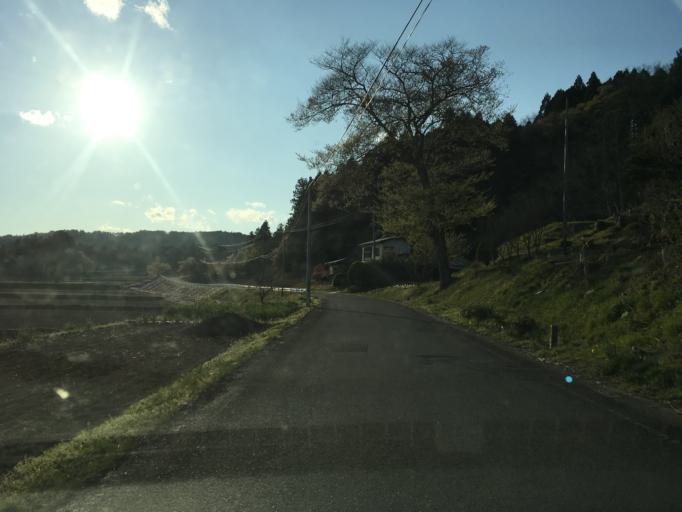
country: JP
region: Iwate
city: Ichinoseki
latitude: 38.8395
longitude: 141.2430
